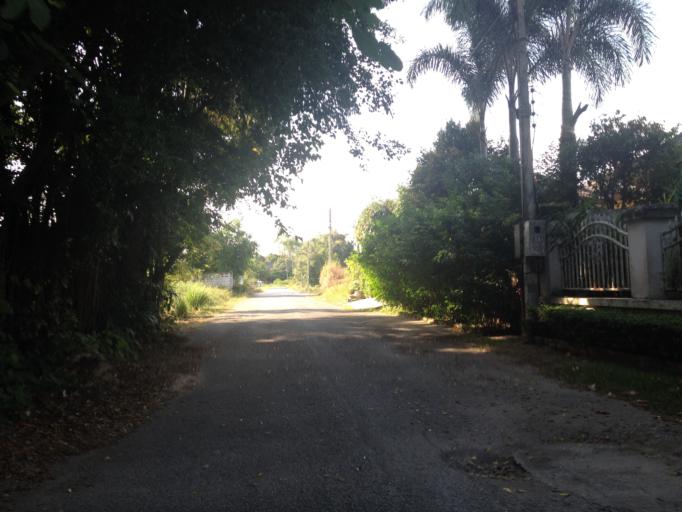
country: TH
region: Chiang Mai
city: Hang Dong
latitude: 18.7002
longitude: 98.9360
